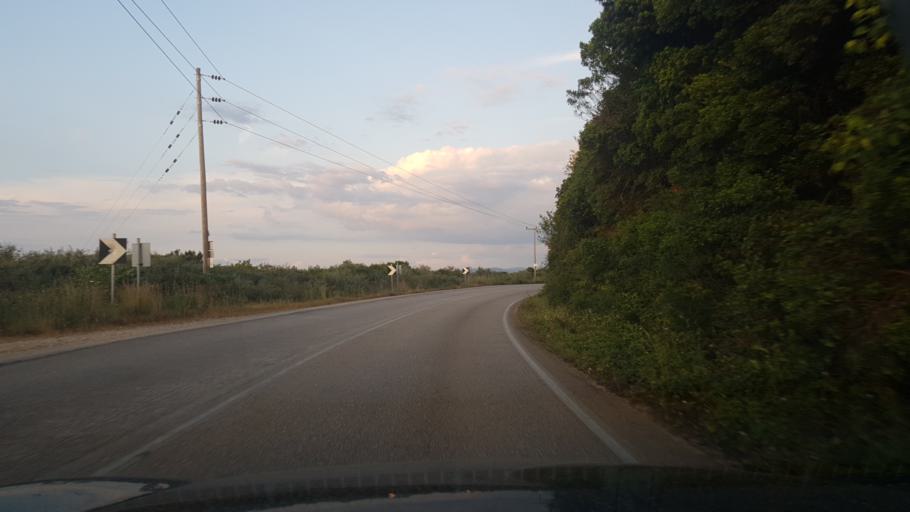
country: GR
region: Ionian Islands
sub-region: Lefkada
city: Lefkada
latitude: 38.8644
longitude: 20.7750
